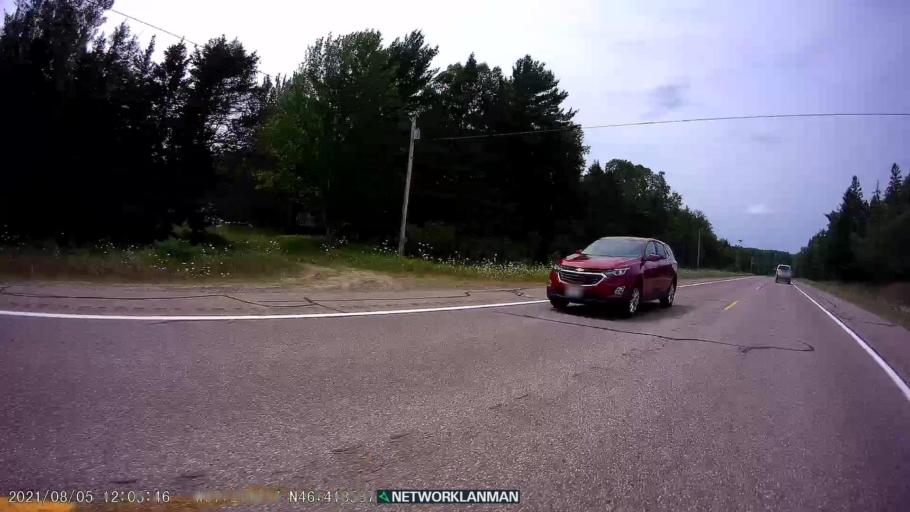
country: US
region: Michigan
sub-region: Marquette County
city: Harvey
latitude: 46.4189
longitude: -87.2598
